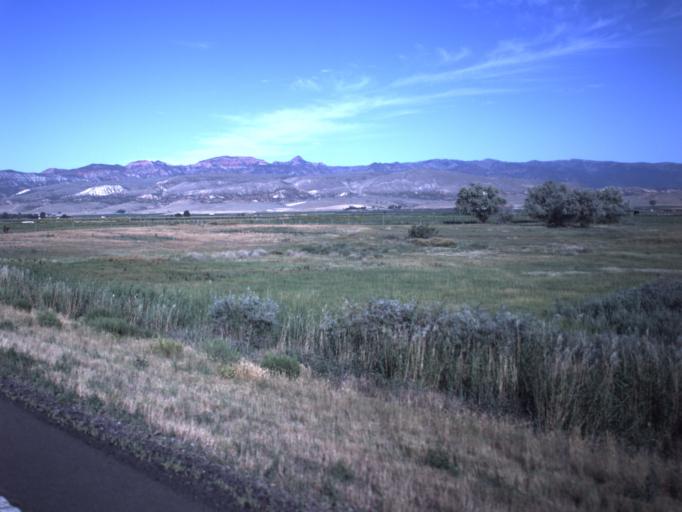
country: US
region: Utah
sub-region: Sevier County
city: Salina
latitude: 38.9376
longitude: -111.8917
